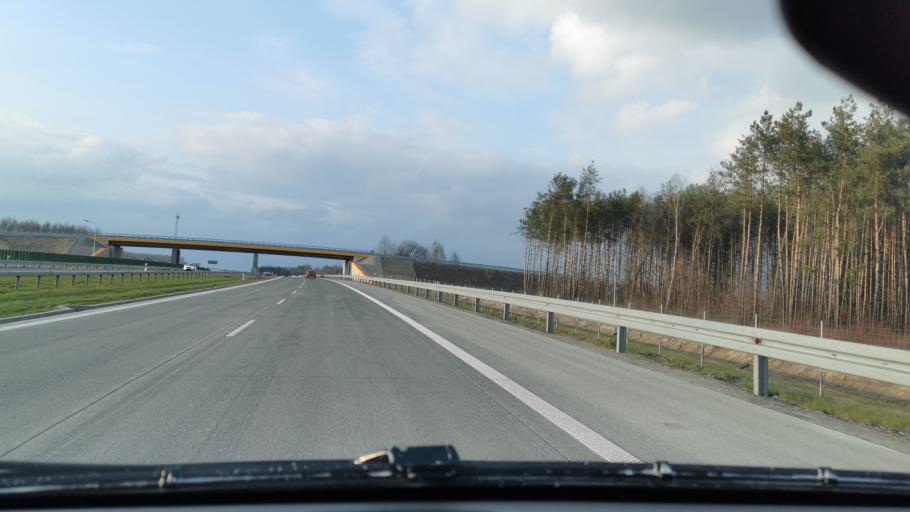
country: PL
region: Masovian Voivodeship
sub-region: Powiat garwolinski
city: Pilawa
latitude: 51.9877
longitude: 21.5504
